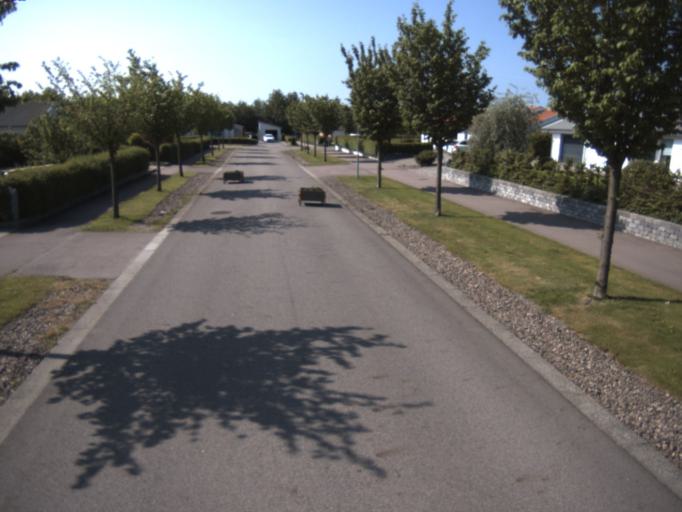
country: SE
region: Skane
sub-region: Helsingborg
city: Rydeback
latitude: 56.0287
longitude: 12.7563
